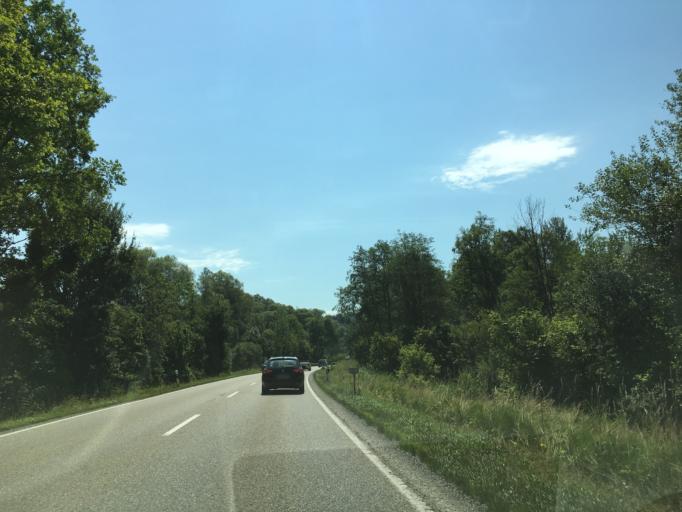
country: DE
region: Bavaria
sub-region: Upper Bavaria
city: Griesstatt
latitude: 47.9970
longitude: 12.1606
